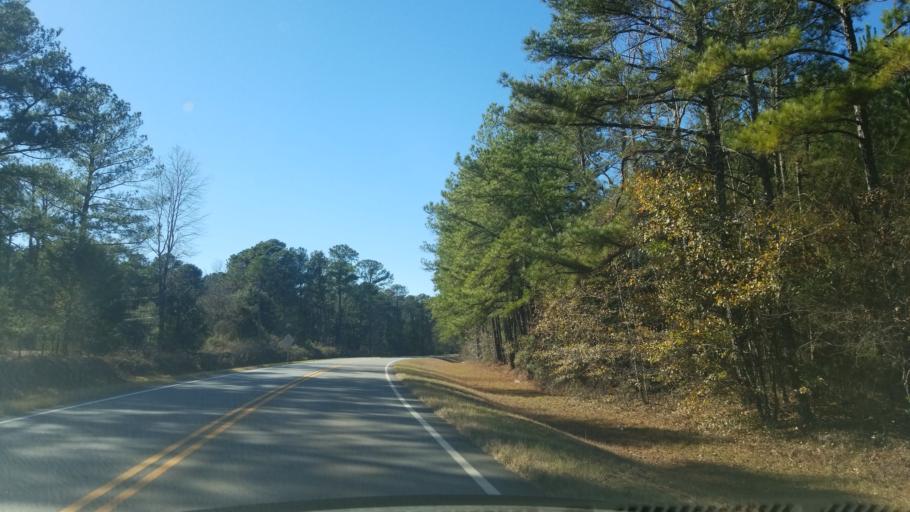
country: US
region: Georgia
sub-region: Talbot County
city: Sardis
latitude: 32.6333
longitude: -84.7260
